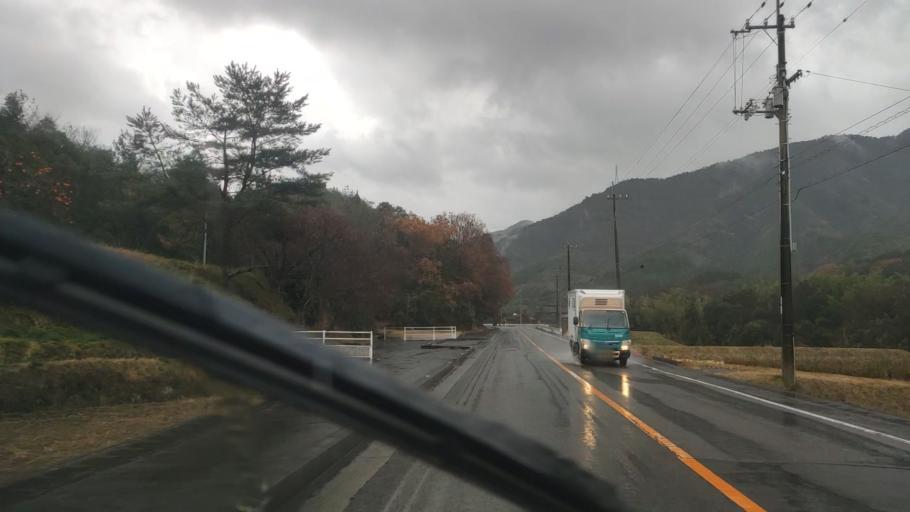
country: JP
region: Tokushima
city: Kamojimacho-jogejima
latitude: 34.2008
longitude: 134.3302
